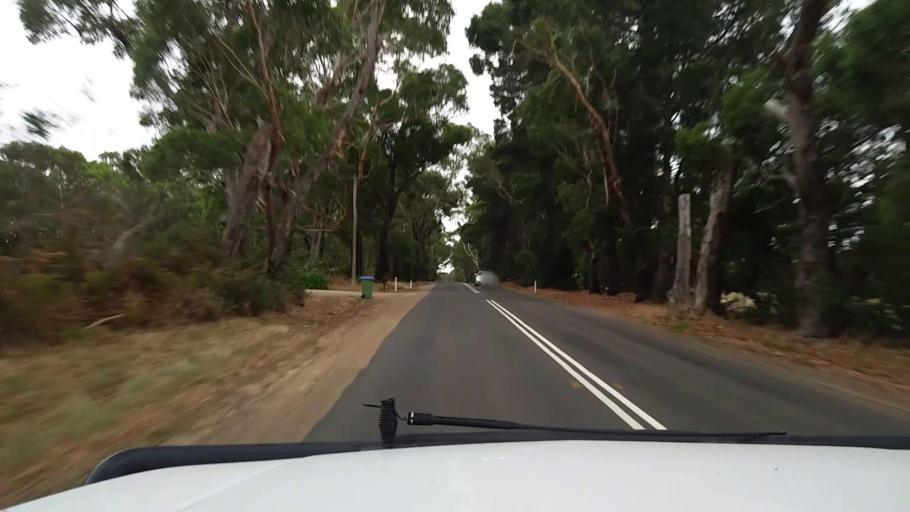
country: AU
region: Victoria
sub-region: Mornington Peninsula
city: Hastings
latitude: -38.3219
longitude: 145.1457
